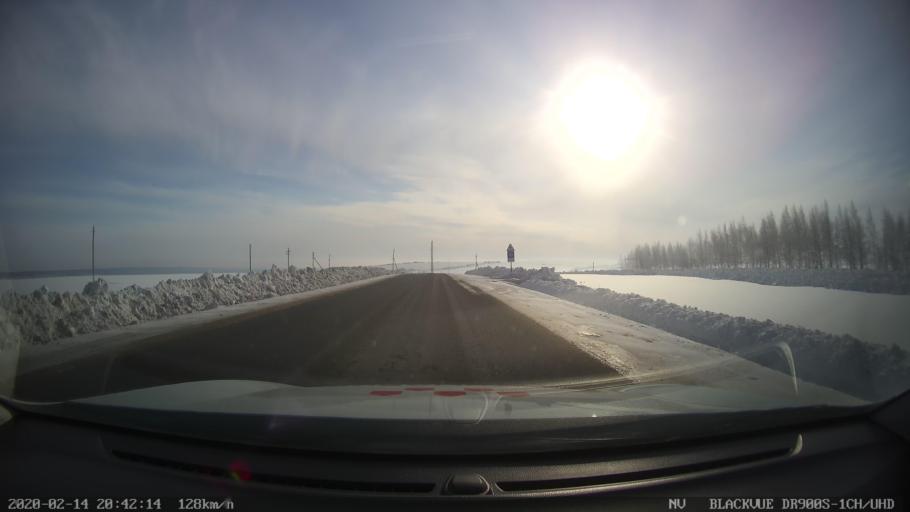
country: RU
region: Tatarstan
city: Kuybyshevskiy Zaton
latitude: 55.3191
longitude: 49.1393
